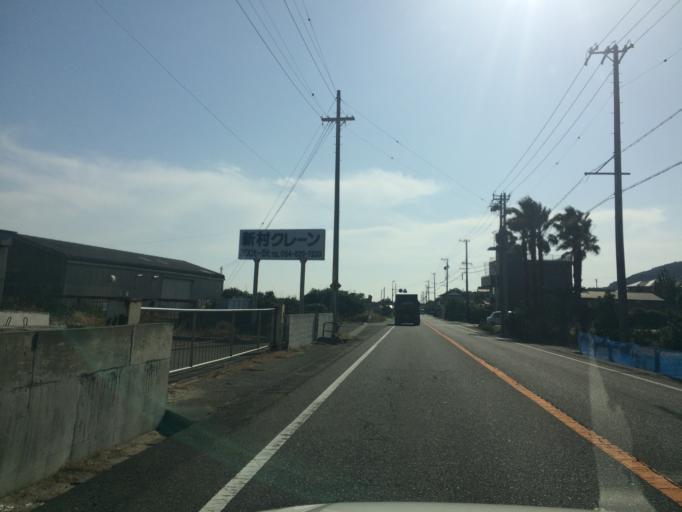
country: JP
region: Shizuoka
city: Sagara
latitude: 34.6612
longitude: 138.1938
